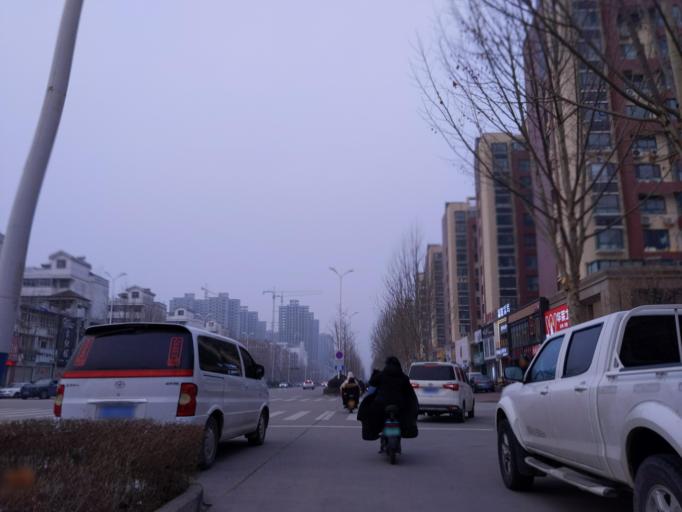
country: CN
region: Henan Sheng
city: Puyang
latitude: 35.7825
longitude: 115.0267
